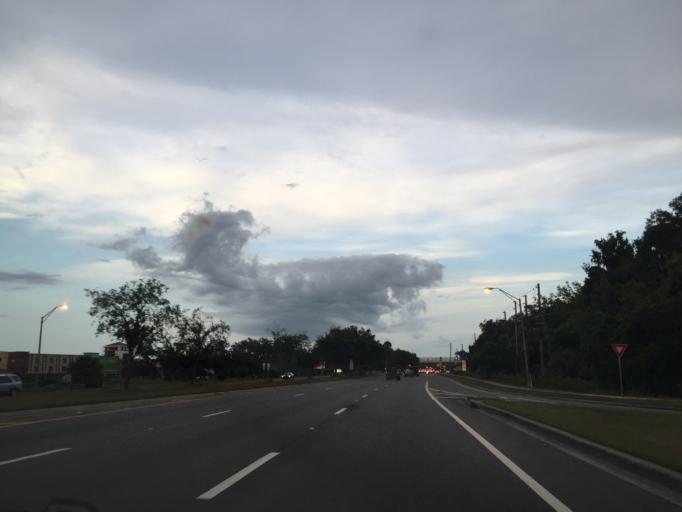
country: US
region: Florida
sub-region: Seminole County
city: Oviedo
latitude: 28.6562
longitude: -81.2311
